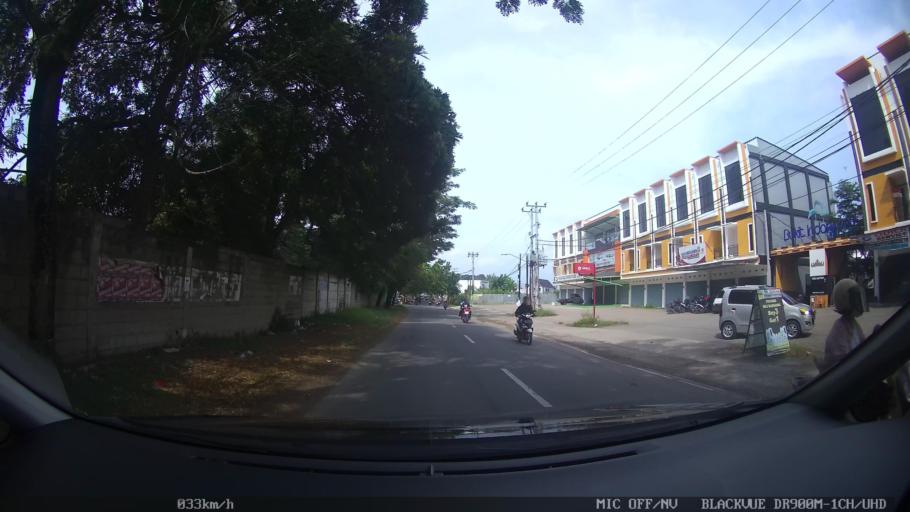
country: ID
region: Lampung
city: Kedaton
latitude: -5.3759
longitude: 105.3070
